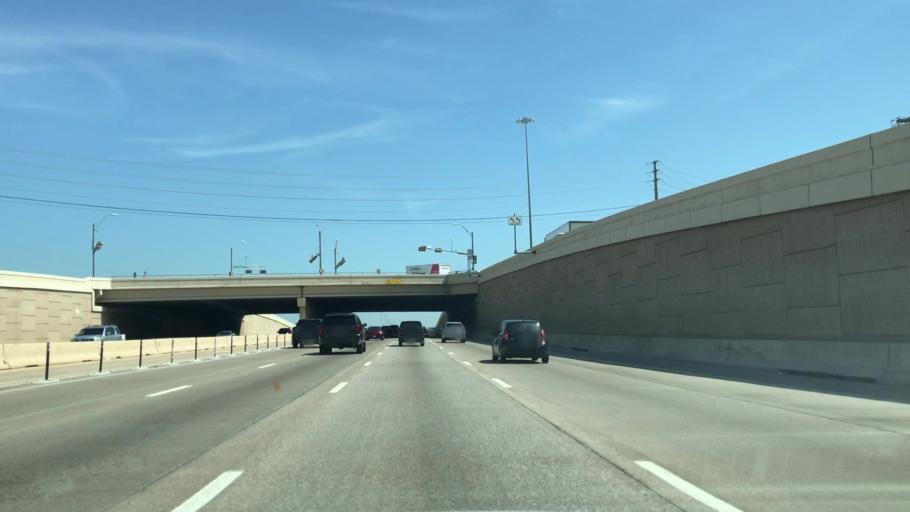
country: US
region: Texas
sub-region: Collin County
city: Plano
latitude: 33.0362
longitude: -96.7050
